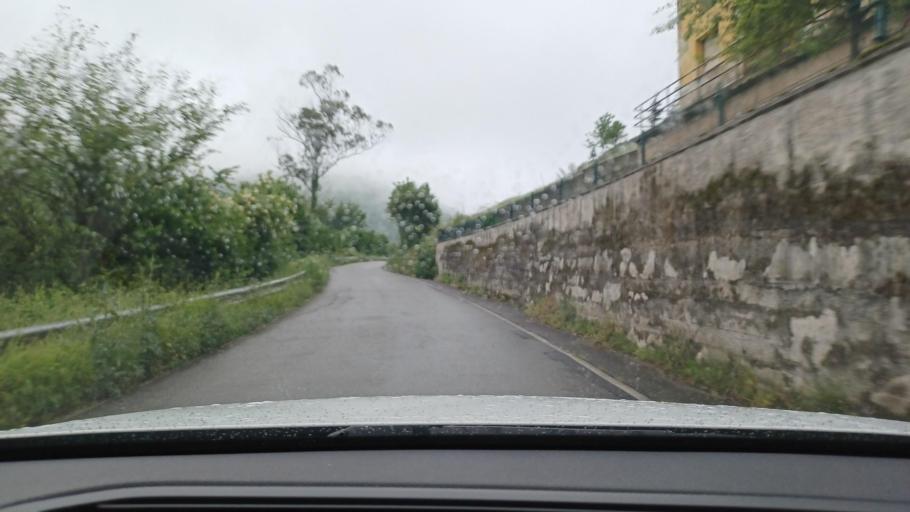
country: ES
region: Asturias
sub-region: Province of Asturias
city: Castandiello
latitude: 43.3017
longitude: -5.9366
